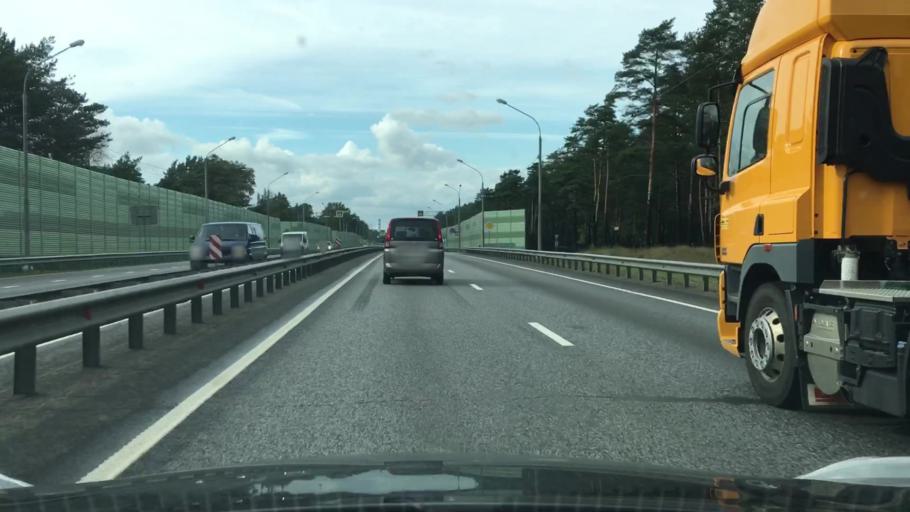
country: RU
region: Tverskaya
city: Radchenko
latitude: 56.6772
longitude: 36.3978
